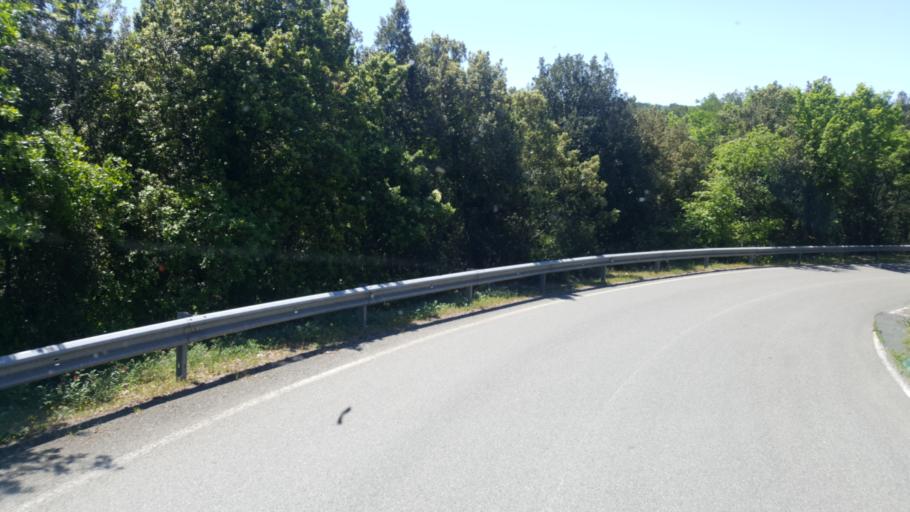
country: IT
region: Tuscany
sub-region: Province of Pisa
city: Castellina Marittima
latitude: 43.4242
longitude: 10.5449
